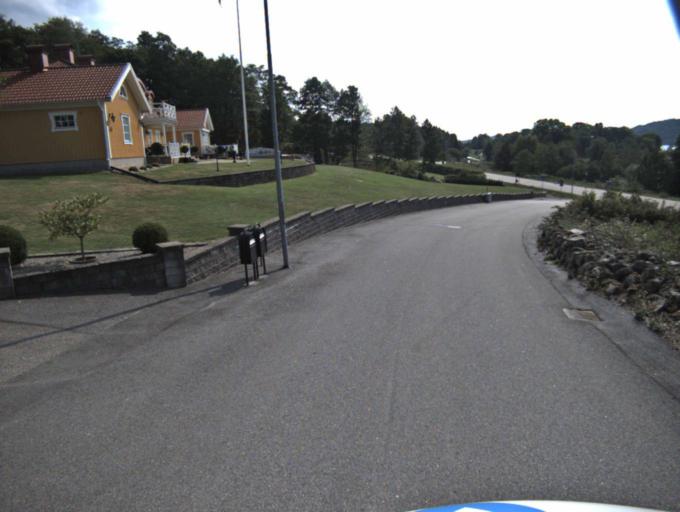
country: SE
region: Vaestra Goetaland
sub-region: Ulricehamns Kommun
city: Ulricehamn
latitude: 57.7738
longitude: 13.4051
